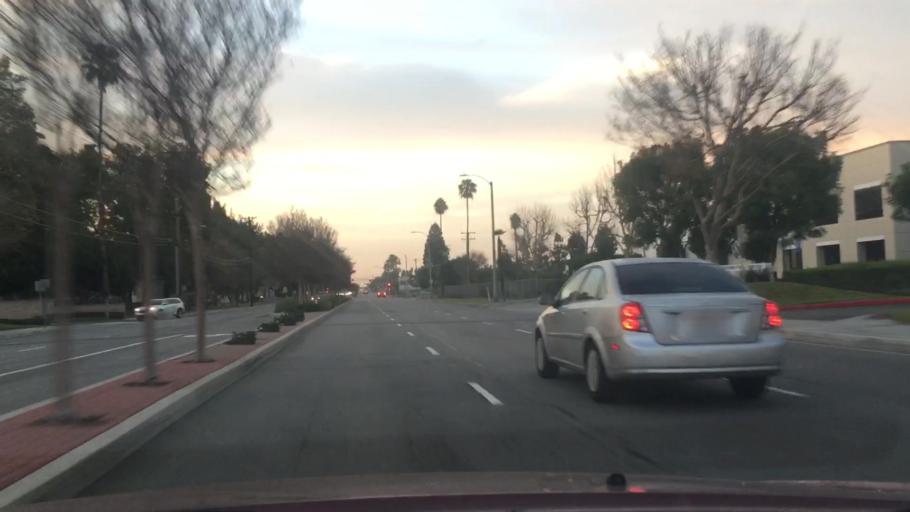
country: US
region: California
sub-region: Orange County
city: Buena Park
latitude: 33.8697
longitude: -118.0114
